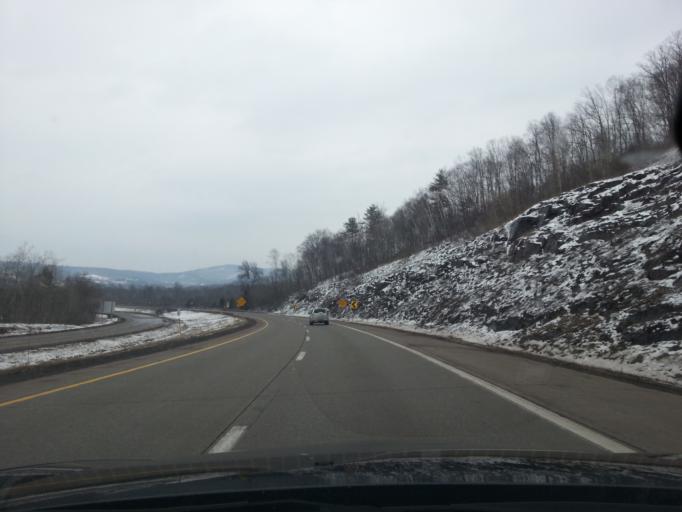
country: US
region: Pennsylvania
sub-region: Luzerne County
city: West Hazleton
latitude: 40.9984
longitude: -76.0108
